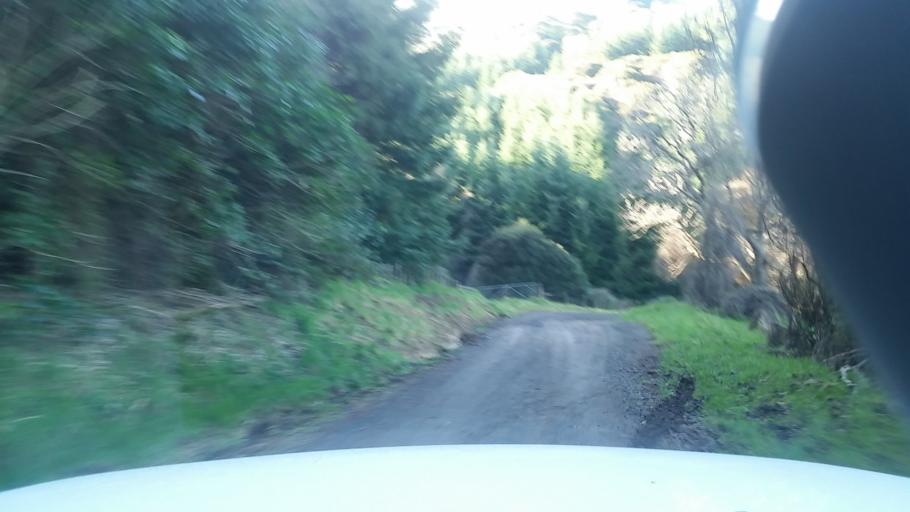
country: NZ
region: Canterbury
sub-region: Christchurch City
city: Christchurch
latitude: -43.7757
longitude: 172.9826
